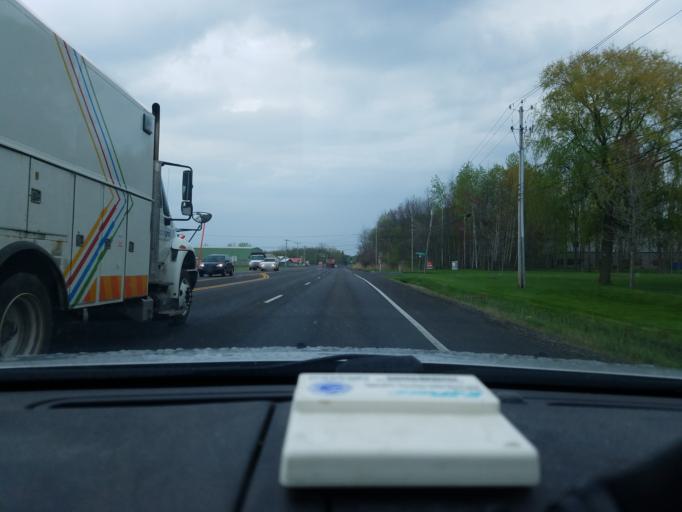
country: US
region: New York
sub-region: Onondaga County
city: North Syracuse
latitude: 43.1252
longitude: -76.0917
